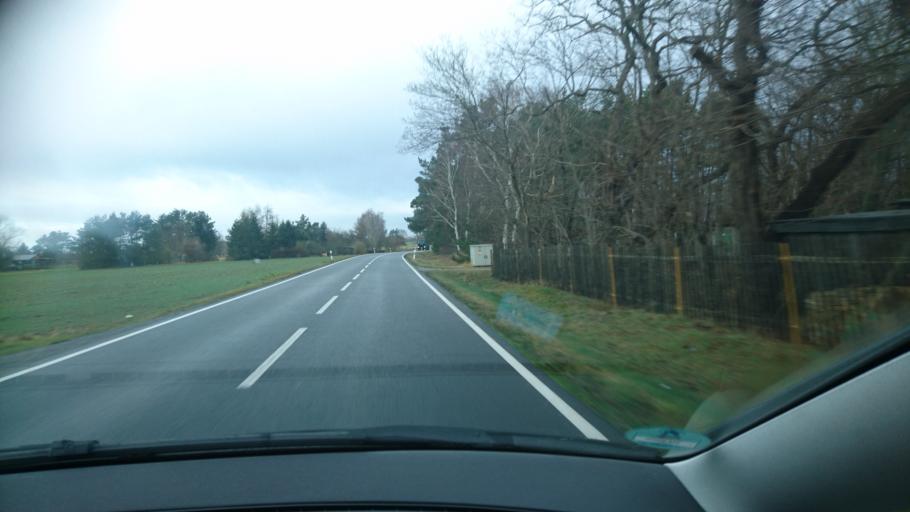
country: DE
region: Saxony
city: Bad Duben
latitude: 51.5847
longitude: 12.6217
